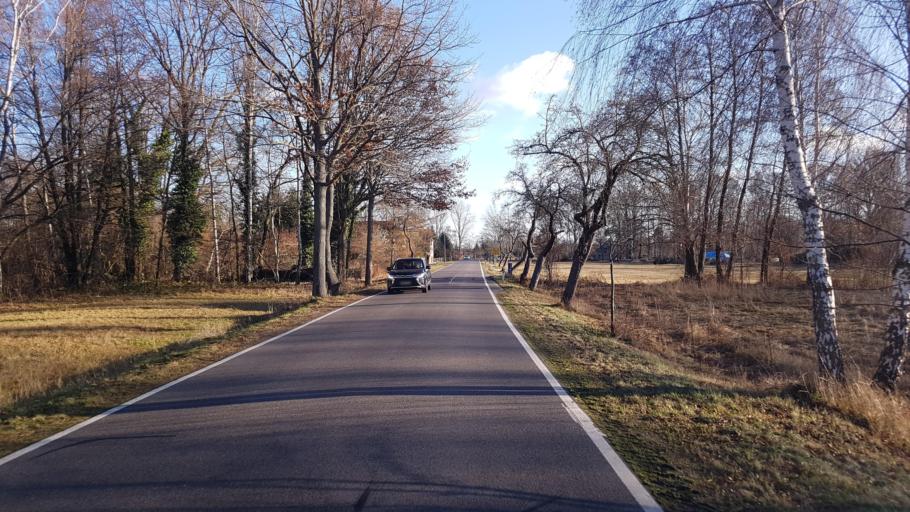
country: DE
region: Brandenburg
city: Forst
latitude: 51.7678
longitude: 14.5867
